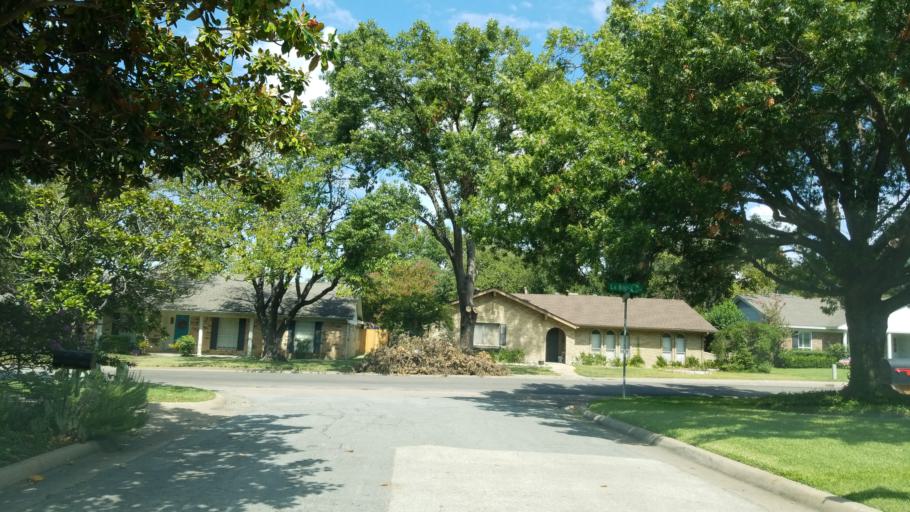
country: US
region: Texas
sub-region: Dallas County
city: Addison
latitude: 32.9643
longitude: -96.7828
